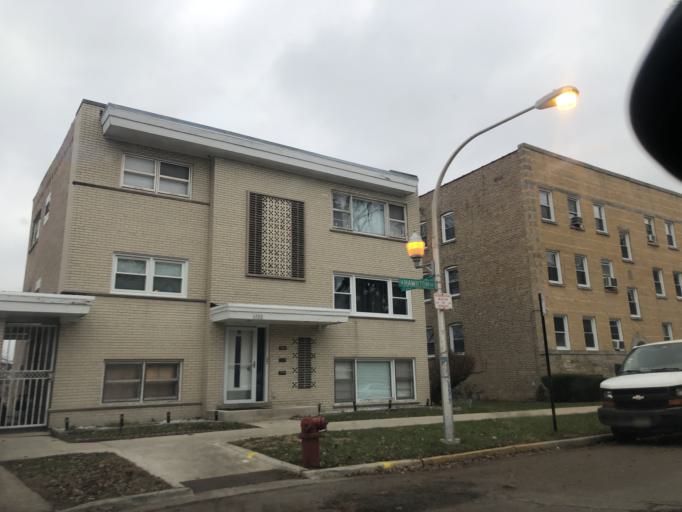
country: US
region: Illinois
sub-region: Cook County
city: Lincolnwood
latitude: 41.9919
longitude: -87.6832
